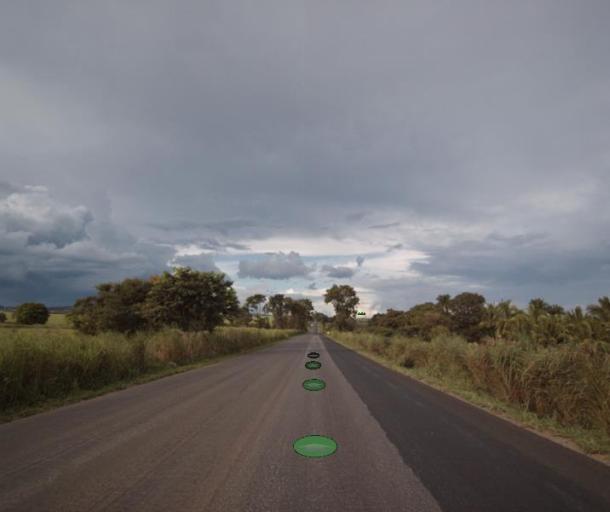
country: BR
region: Goias
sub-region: Ceres
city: Ceres
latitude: -15.1374
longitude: -49.5218
